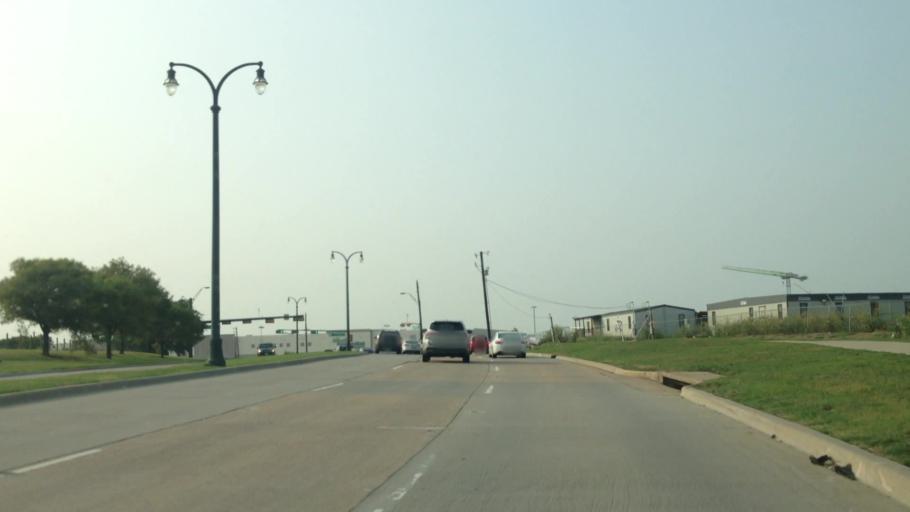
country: US
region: Texas
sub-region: Denton County
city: The Colony
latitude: 33.0663
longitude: -96.8613
